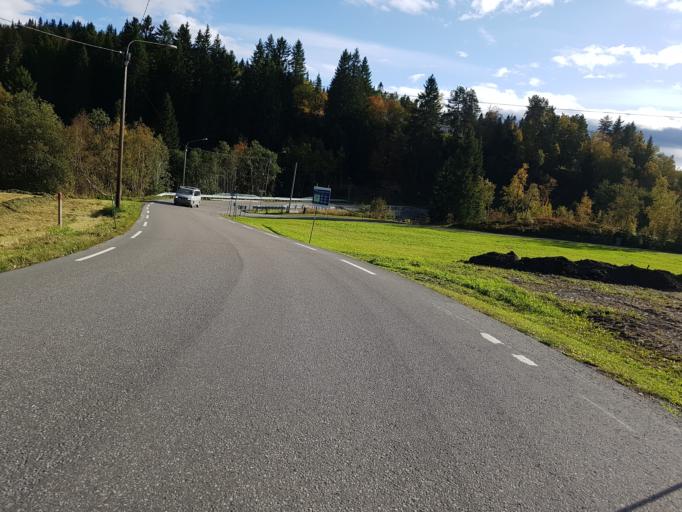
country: NO
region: Sor-Trondelag
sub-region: Klaebu
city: Klaebu
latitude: 63.3998
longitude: 10.5234
